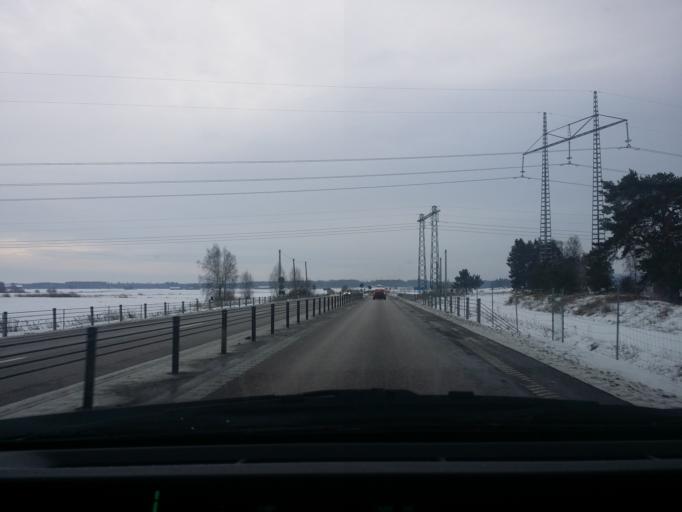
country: SE
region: Vaestra Goetaland
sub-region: Skovde Kommun
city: Stopen
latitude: 58.5641
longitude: 13.8006
